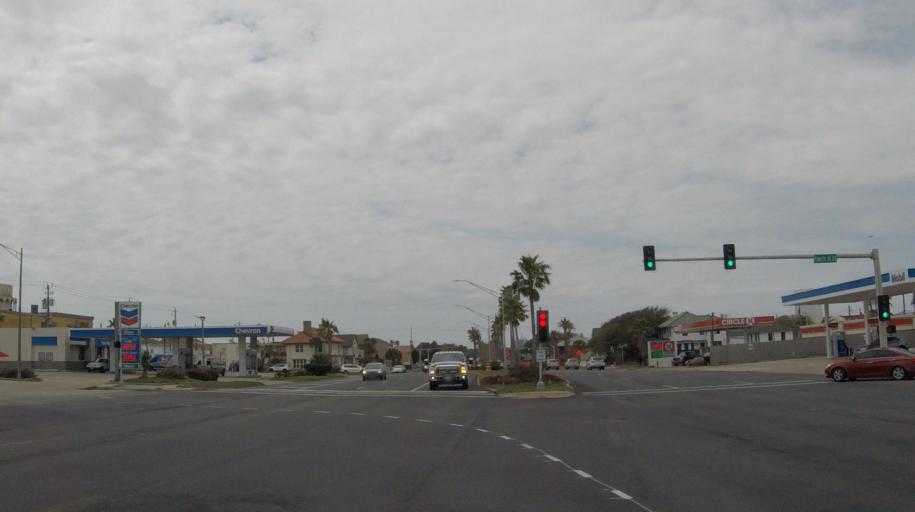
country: US
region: Texas
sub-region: Galveston County
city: Galveston
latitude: 29.3052
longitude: -94.7724
